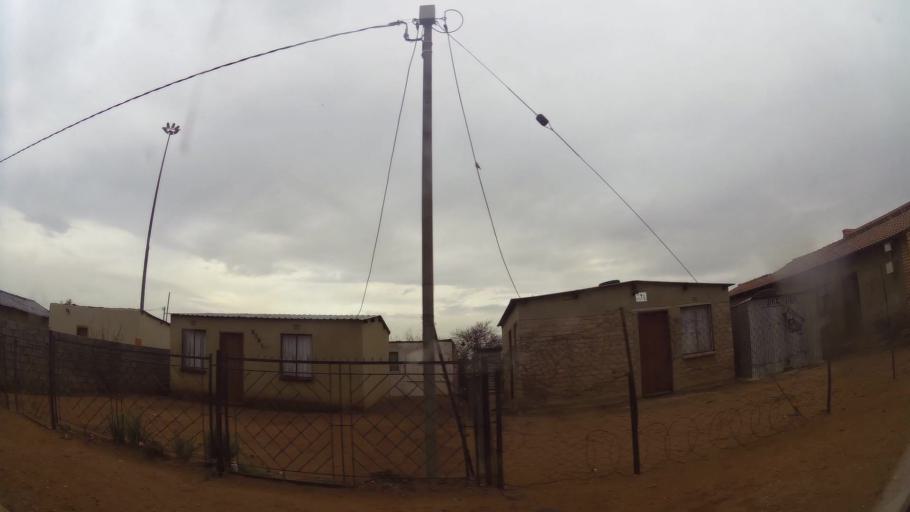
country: ZA
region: Gauteng
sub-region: Ekurhuleni Metropolitan Municipality
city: Germiston
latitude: -26.3763
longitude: 28.1756
